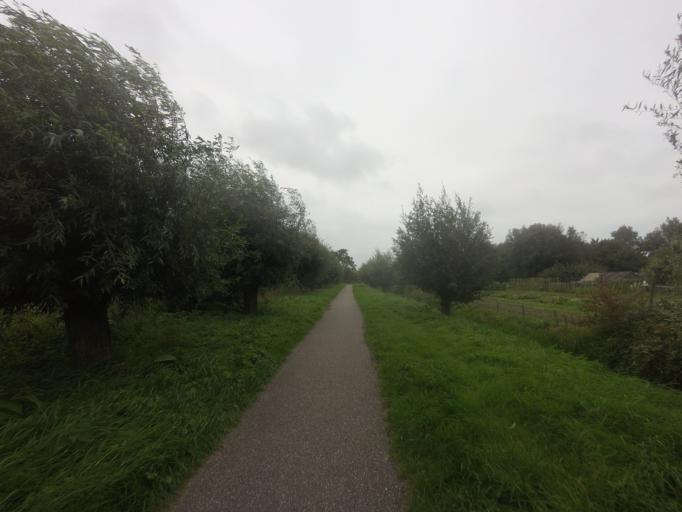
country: NL
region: Friesland
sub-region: Gemeente Leeuwarden
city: Bilgaard
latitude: 53.2252
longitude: 5.7924
